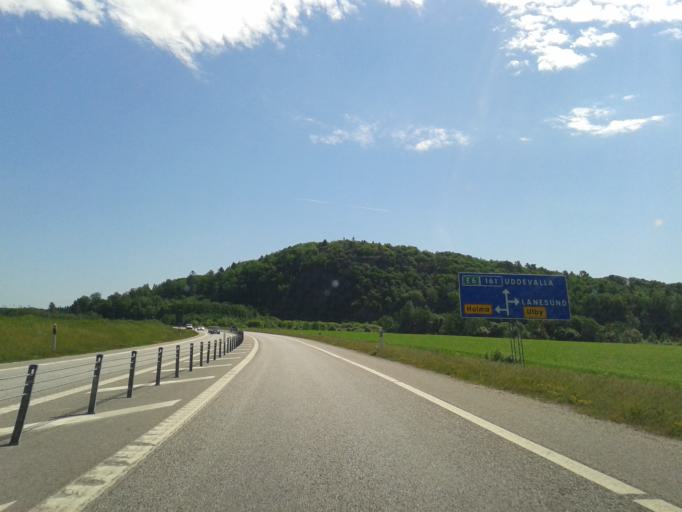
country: SE
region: Vaestra Goetaland
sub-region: Orust
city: Henan
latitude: 58.3468
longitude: 11.7517
